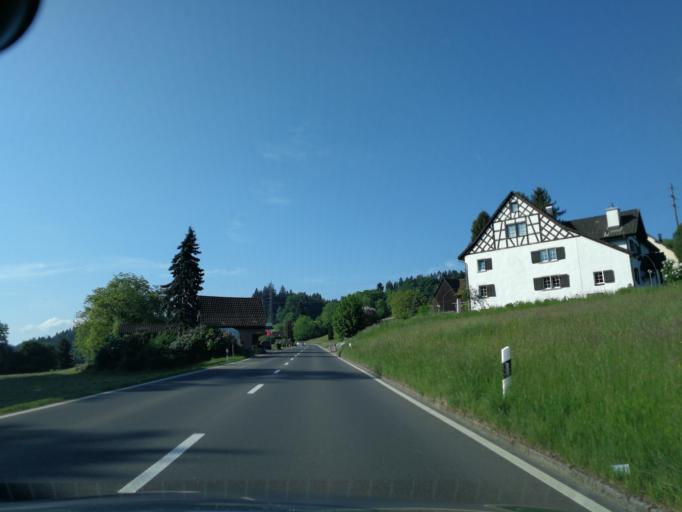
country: CH
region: Zurich
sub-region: Bezirk Horgen
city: Horgen / Allmend
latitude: 47.2336
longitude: 8.6143
